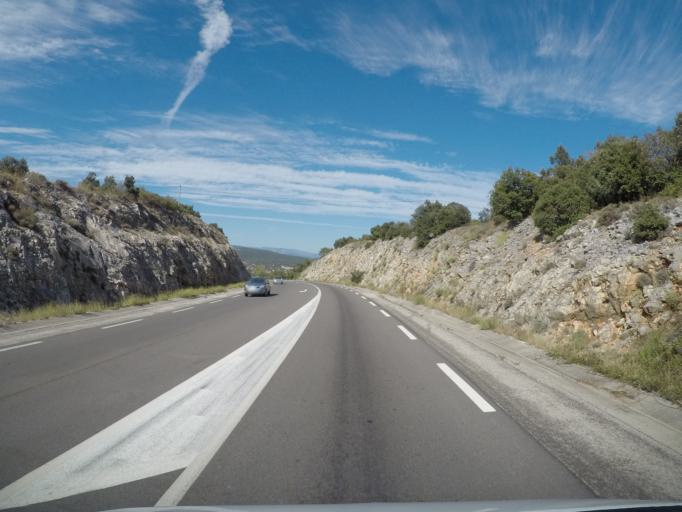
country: FR
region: Languedoc-Roussillon
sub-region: Departement de l'Herault
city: Saint-Martin-de-Londres
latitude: 43.7712
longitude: 3.7462
